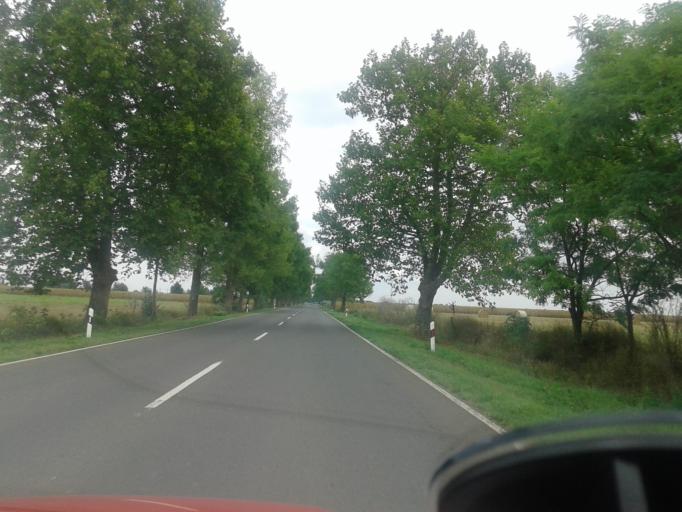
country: HU
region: Csongrad
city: Roszke
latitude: 46.2064
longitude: 20.0422
